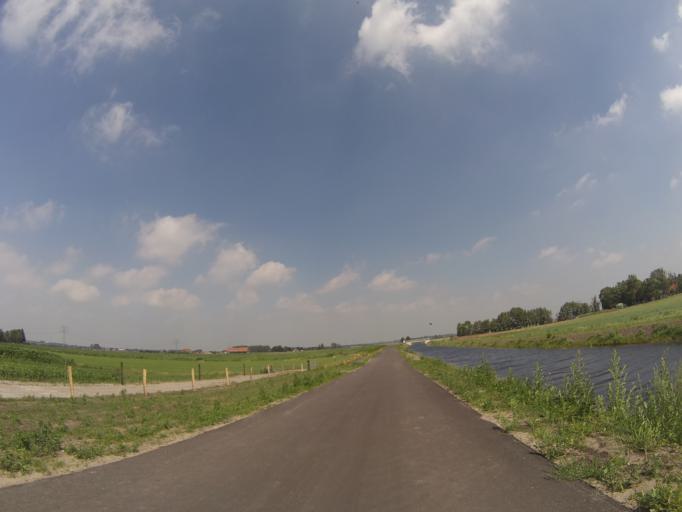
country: NL
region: Utrecht
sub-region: Gemeente Bunschoten
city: Bunschoten
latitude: 52.2245
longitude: 5.3946
